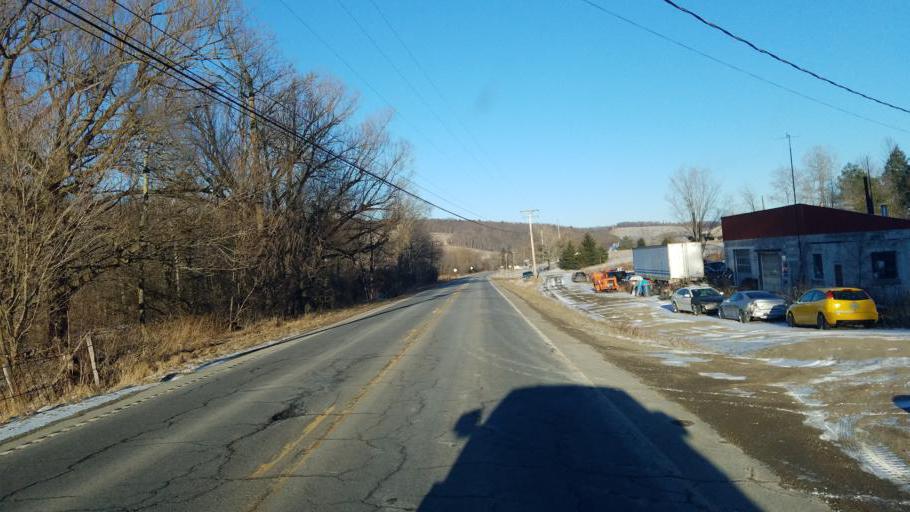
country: US
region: Pennsylvania
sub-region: Tioga County
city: Westfield
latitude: 41.9442
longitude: -77.6976
